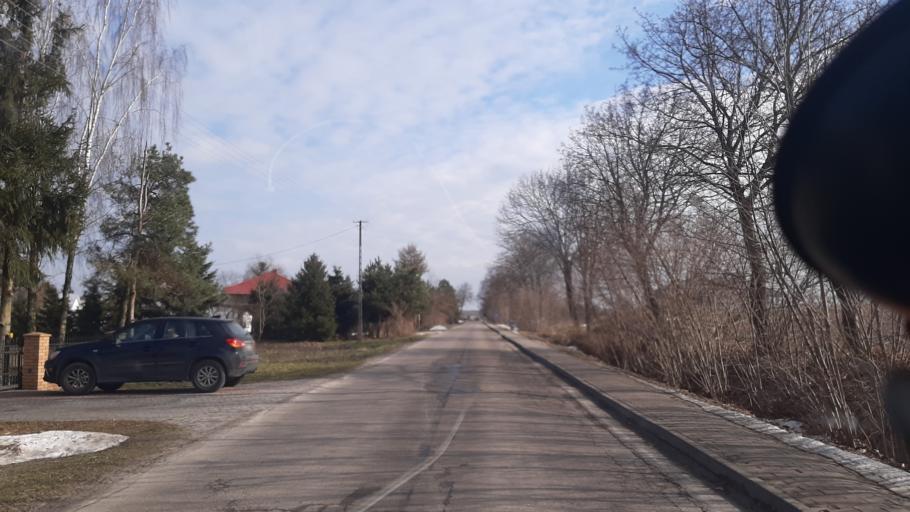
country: PL
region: Lublin Voivodeship
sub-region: Powiat lubartowski
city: Uscimow Stary
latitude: 51.4710
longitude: 22.9493
